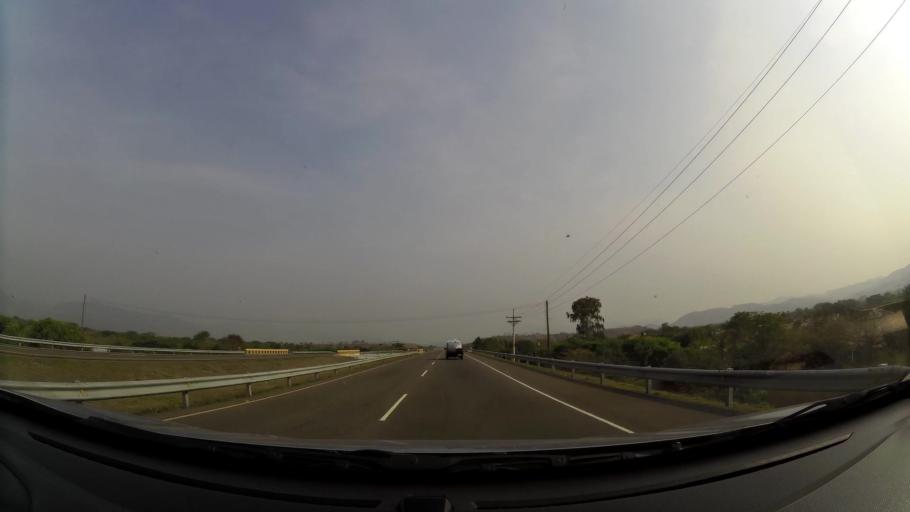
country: HN
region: Comayagua
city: Comayagua
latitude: 14.4403
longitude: -87.6589
